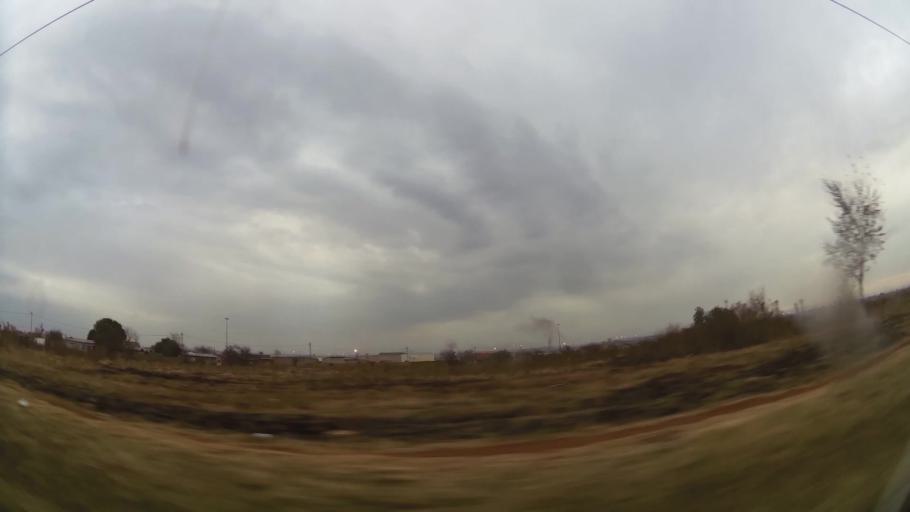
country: ZA
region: Gauteng
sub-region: Ekurhuleni Metropolitan Municipality
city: Germiston
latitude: -26.3708
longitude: 28.1842
